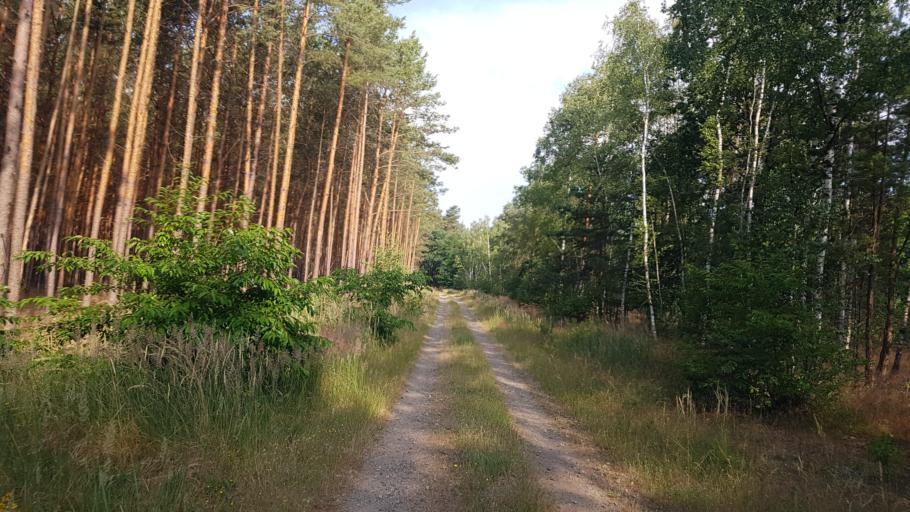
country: DE
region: Brandenburg
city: Niedergorsdorf
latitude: 52.0306
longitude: 12.9541
